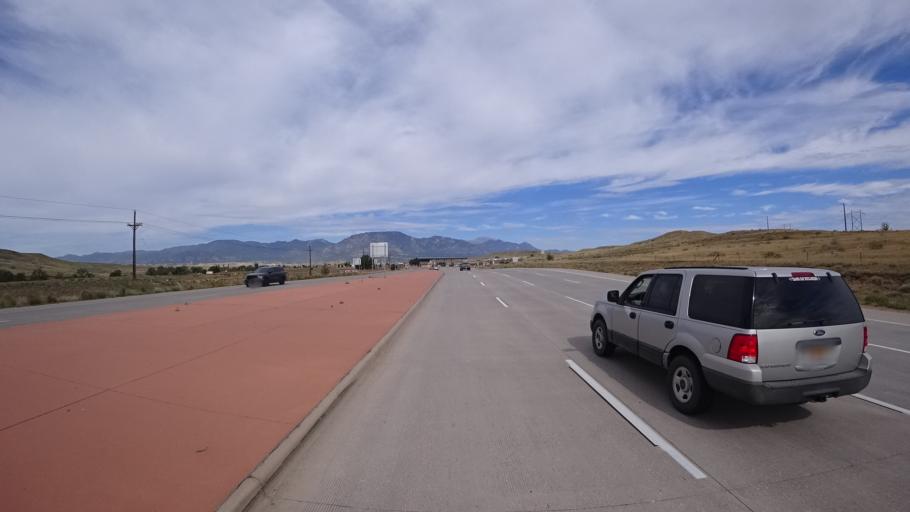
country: US
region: Colorado
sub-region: El Paso County
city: Security-Widefield
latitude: 38.7249
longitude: -104.7370
